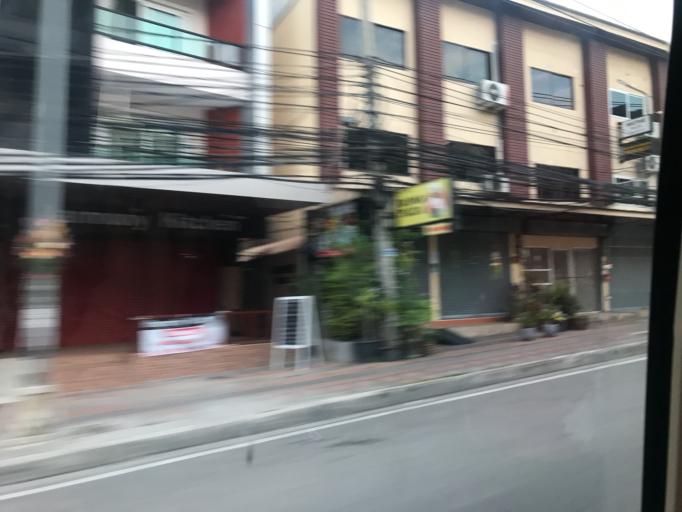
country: TH
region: Chon Buri
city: Phatthaya
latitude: 12.9152
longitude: 100.8712
